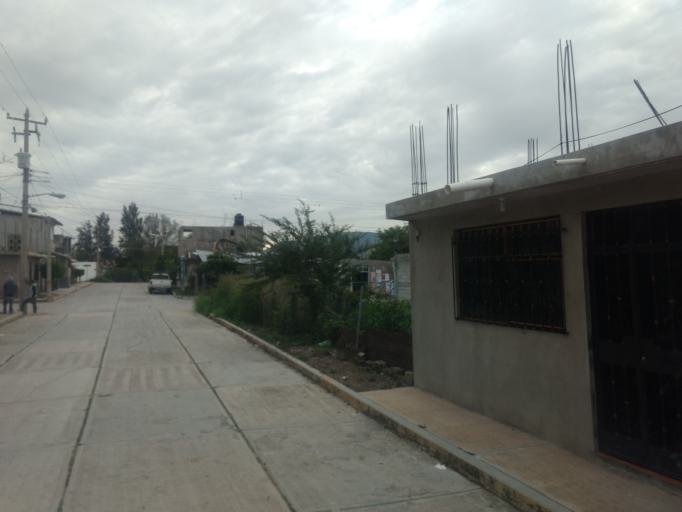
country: MX
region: Oaxaca
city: Ciudad de Huajuapam de Leon
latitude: 17.8058
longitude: -97.7909
